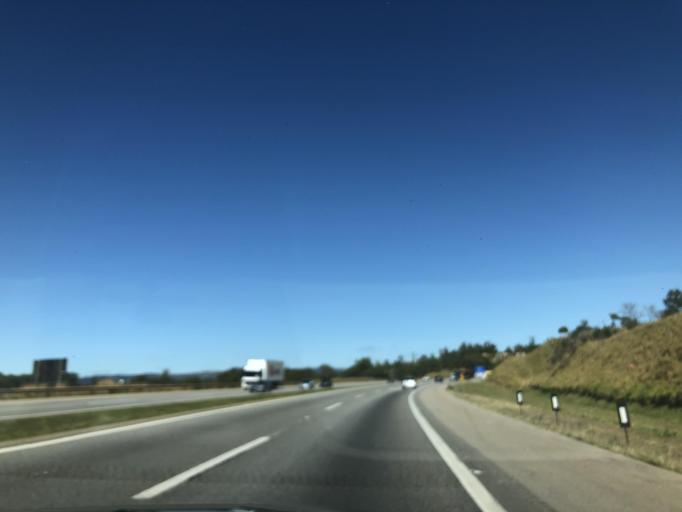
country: BR
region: Sao Paulo
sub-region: Sorocaba
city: Sorocaba
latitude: -23.4735
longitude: -47.3809
